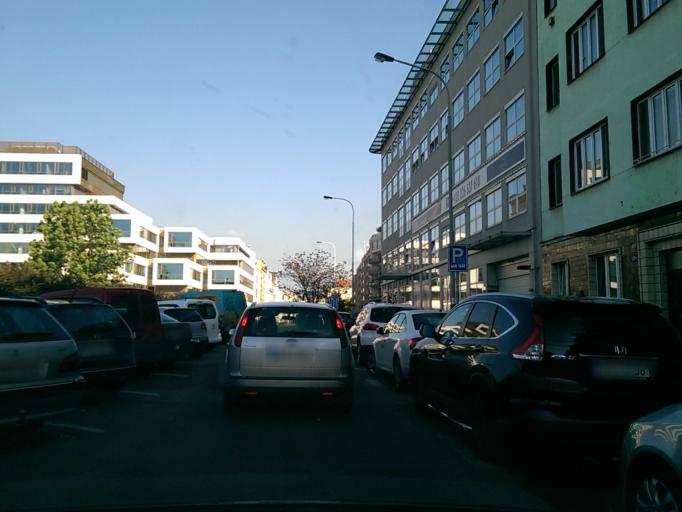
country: CZ
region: Praha
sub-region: Praha 2
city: Vysehrad
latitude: 50.0602
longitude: 14.4284
